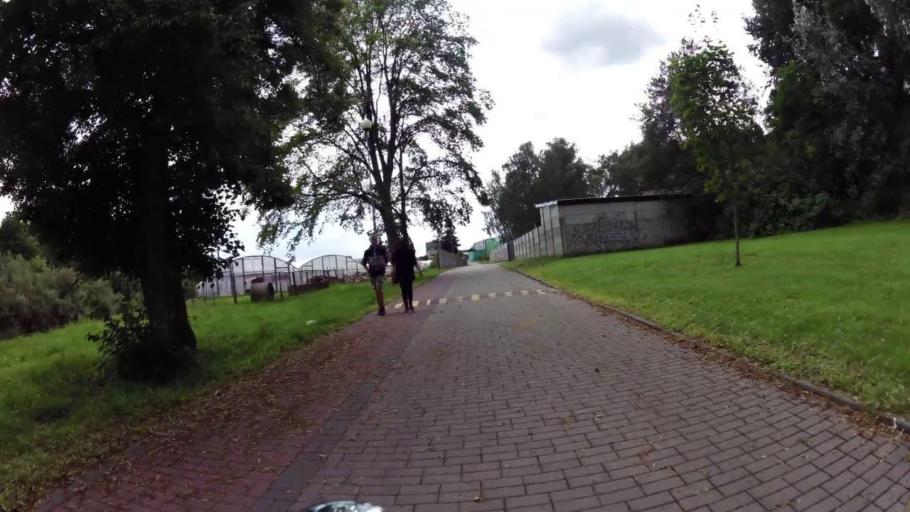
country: PL
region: West Pomeranian Voivodeship
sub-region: Powiat bialogardzki
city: Karlino
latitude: 54.0400
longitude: 15.8826
